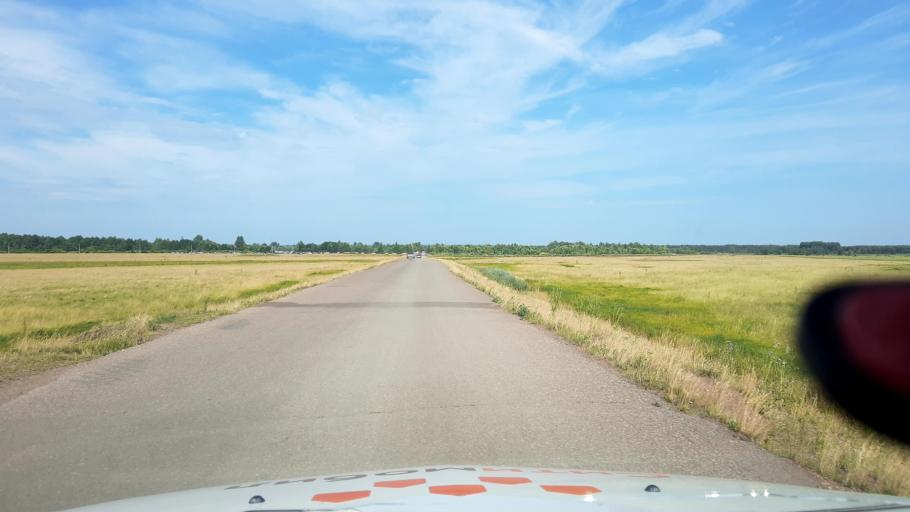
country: RU
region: Bashkortostan
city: Mikhaylovka
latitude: 54.9646
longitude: 55.8023
